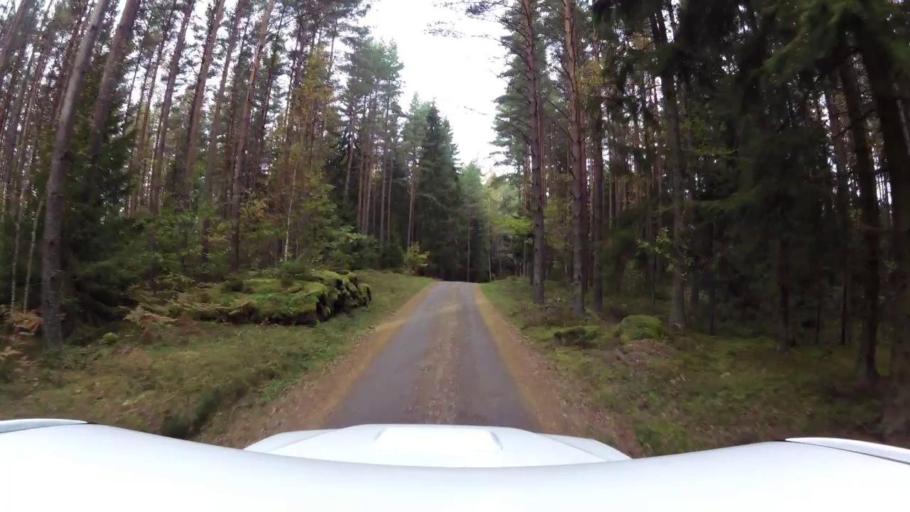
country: SE
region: OEstergoetland
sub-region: Linkopings Kommun
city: Ekangen
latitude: 58.5560
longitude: 15.6712
